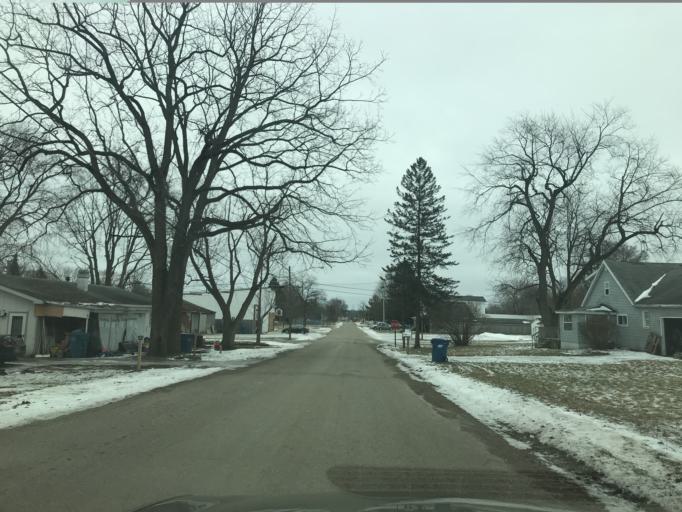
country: US
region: Michigan
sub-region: Jackson County
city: Brooklyn
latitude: 42.0699
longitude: -84.3325
